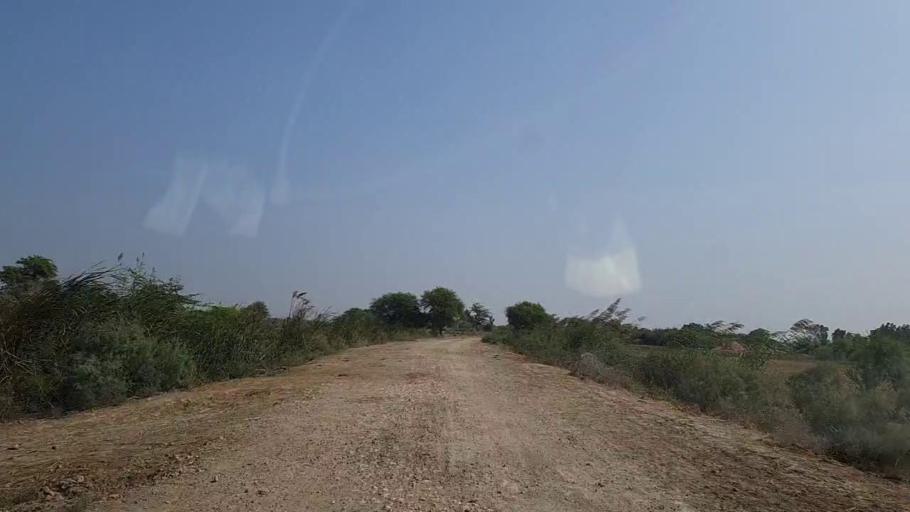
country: PK
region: Sindh
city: Mirpur Sakro
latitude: 24.5300
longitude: 67.7926
